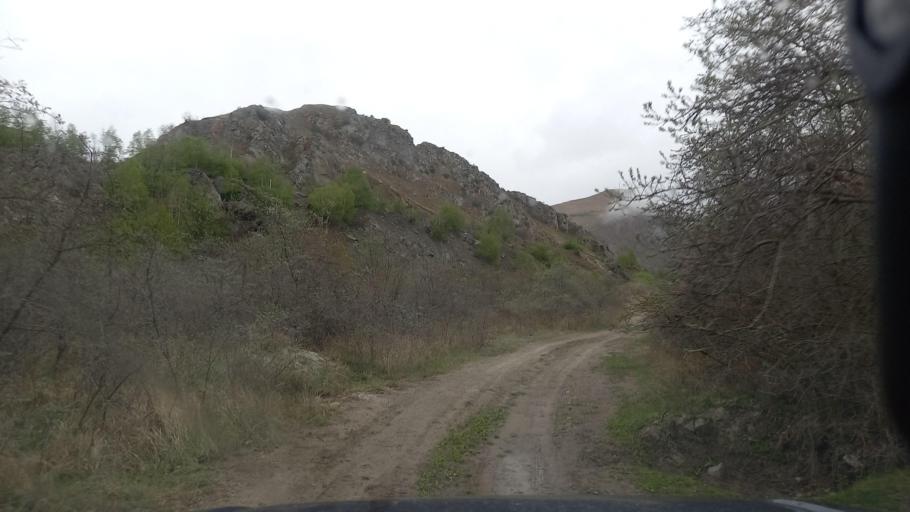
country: RU
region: Kabardino-Balkariya
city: Bylym
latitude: 43.4558
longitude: 42.9995
